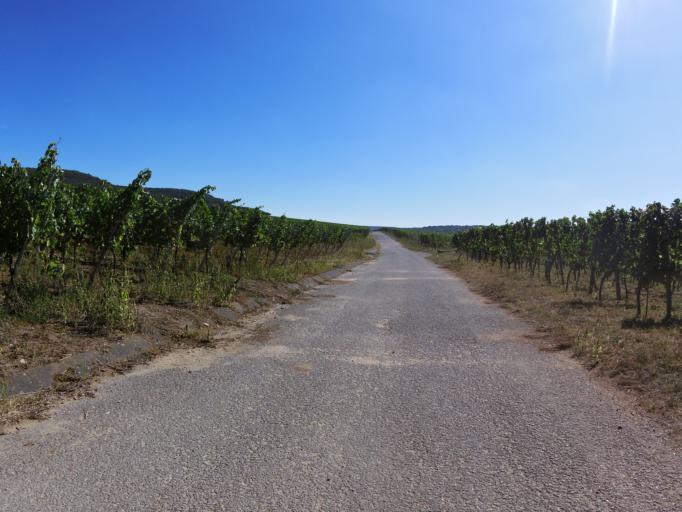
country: DE
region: Bavaria
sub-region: Regierungsbezirk Unterfranken
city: Thungersheim
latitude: 49.8718
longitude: 9.8489
